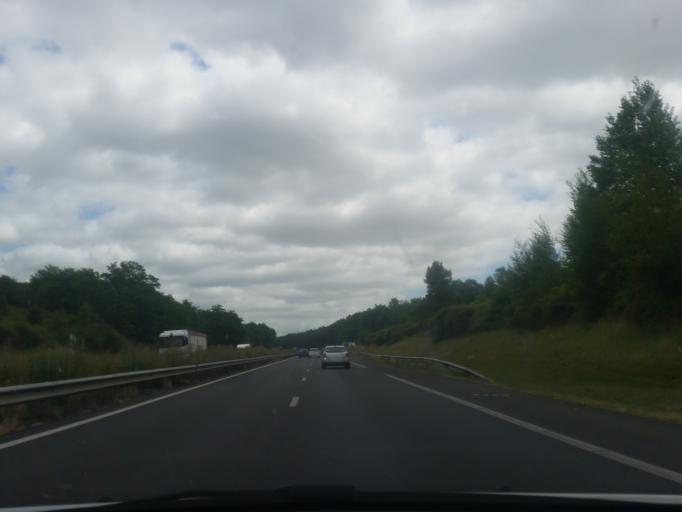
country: FR
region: Pays de la Loire
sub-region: Departement de Maine-et-Loire
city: Corze
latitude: 47.5199
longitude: -0.3680
